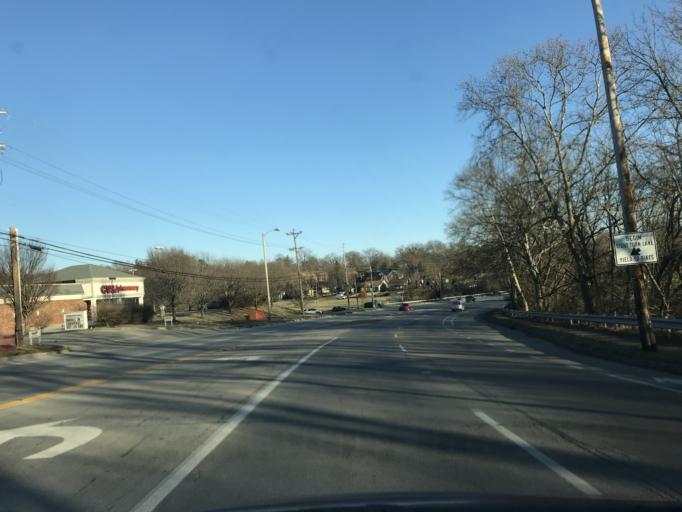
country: US
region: Kentucky
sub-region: Jefferson County
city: Audubon Park
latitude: 38.2110
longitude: -85.7182
